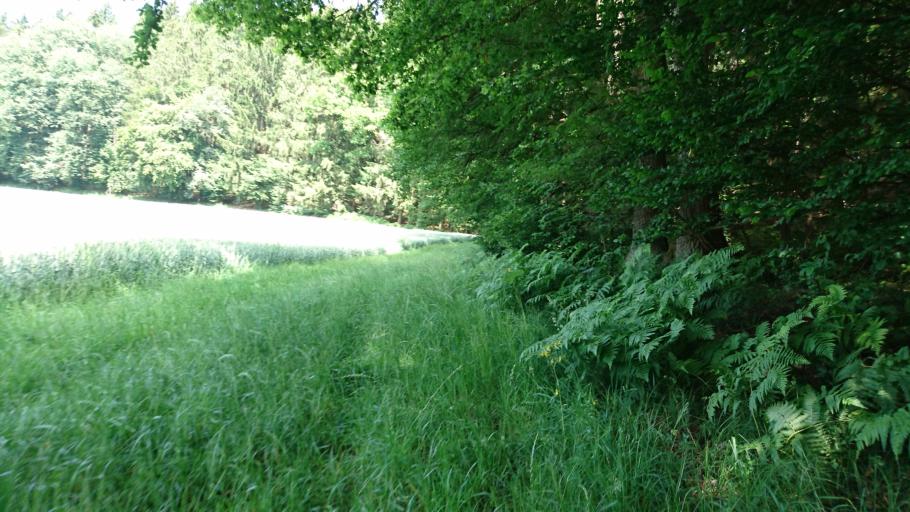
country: DE
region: Bavaria
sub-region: Swabia
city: Zusmarshausen
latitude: 48.4306
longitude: 10.6088
